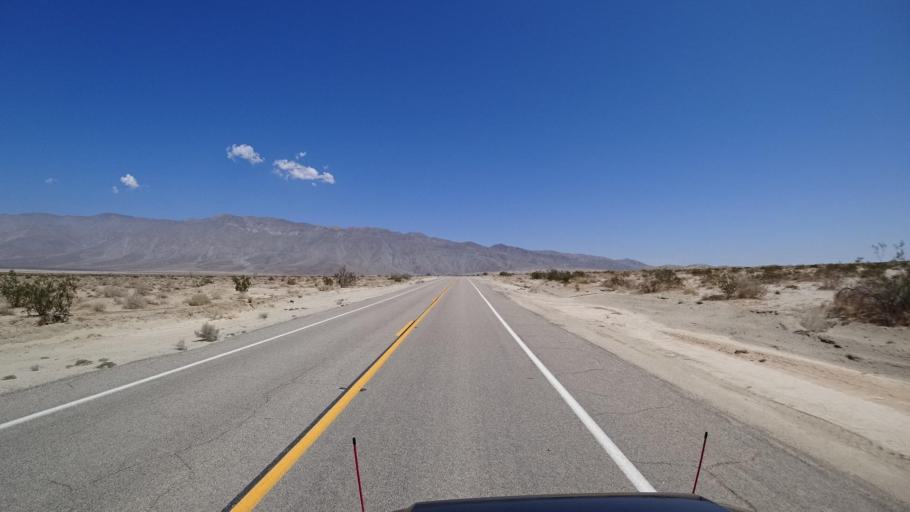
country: US
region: California
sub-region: San Diego County
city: Borrego Springs
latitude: 33.3001
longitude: -116.2694
